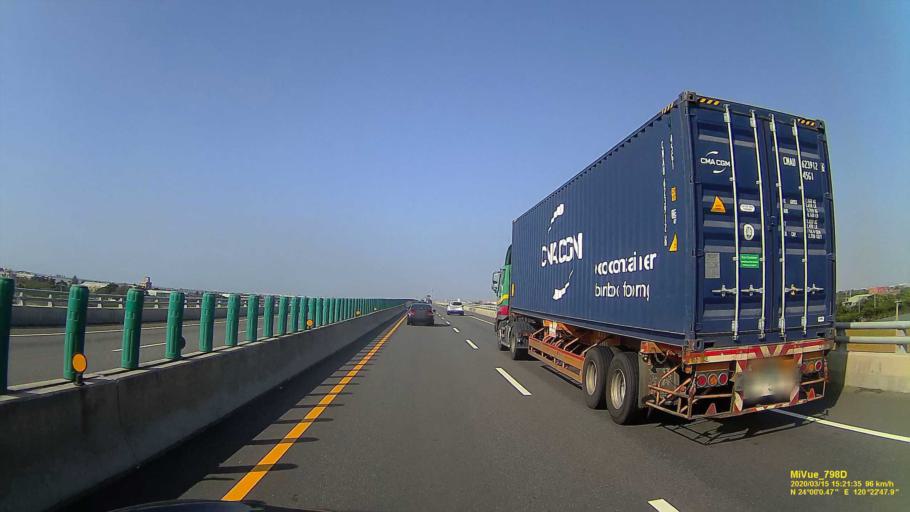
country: TW
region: Taiwan
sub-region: Changhua
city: Chang-hua
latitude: 24.0012
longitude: 120.3803
